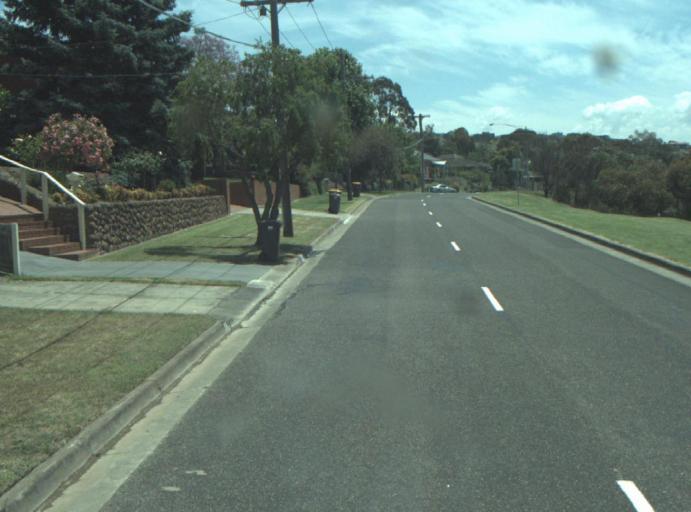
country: AU
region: Victoria
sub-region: Greater Geelong
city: Wandana Heights
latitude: -38.1658
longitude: 144.3255
